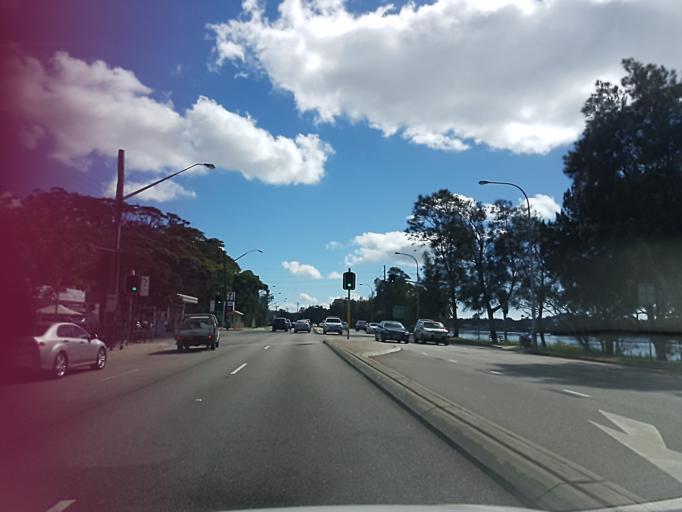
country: AU
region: New South Wales
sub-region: Pittwater
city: North Narrabeen
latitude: -33.7082
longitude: 151.2964
